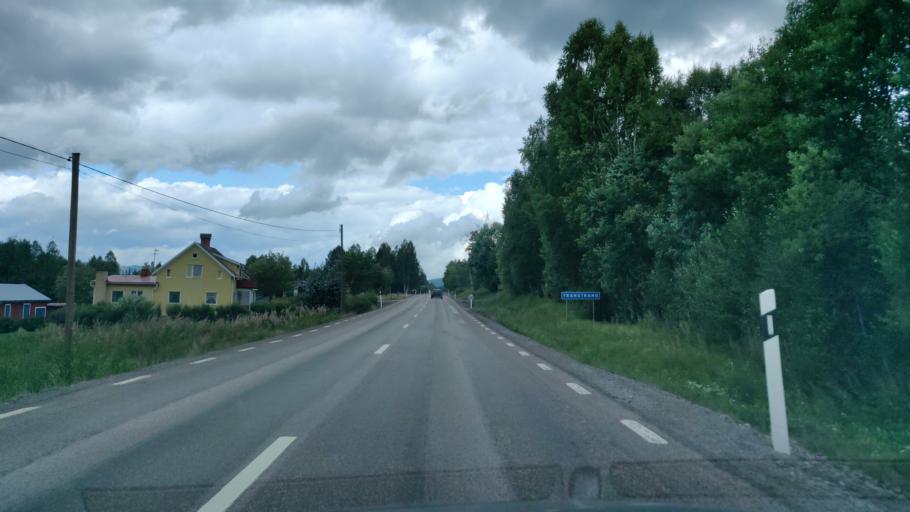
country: SE
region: Vaermland
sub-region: Torsby Kommun
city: Torsby
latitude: 60.5851
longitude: 13.0801
